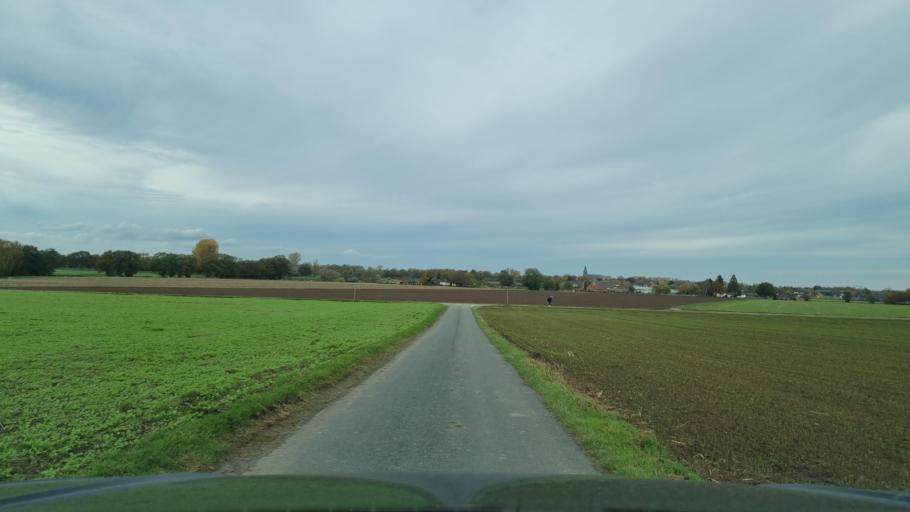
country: DE
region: North Rhine-Westphalia
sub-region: Regierungsbezirk Dusseldorf
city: Kranenburg
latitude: 51.7751
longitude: 6.0016
